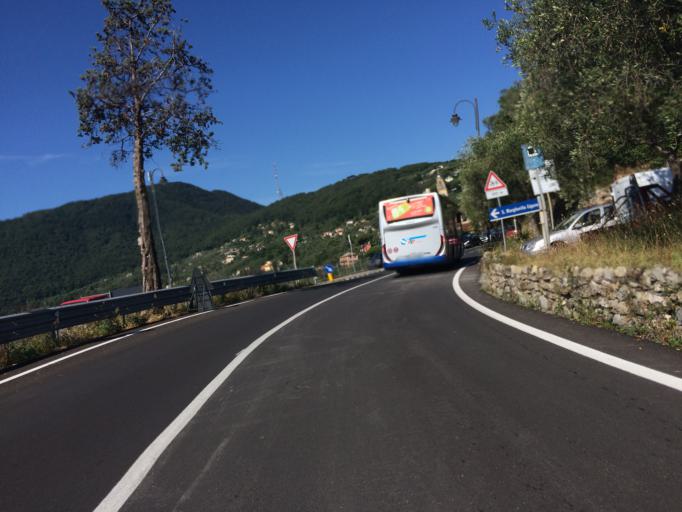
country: IT
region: Liguria
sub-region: Provincia di Genova
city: Santa Margherita Ligure
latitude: 44.3397
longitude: 9.1912
